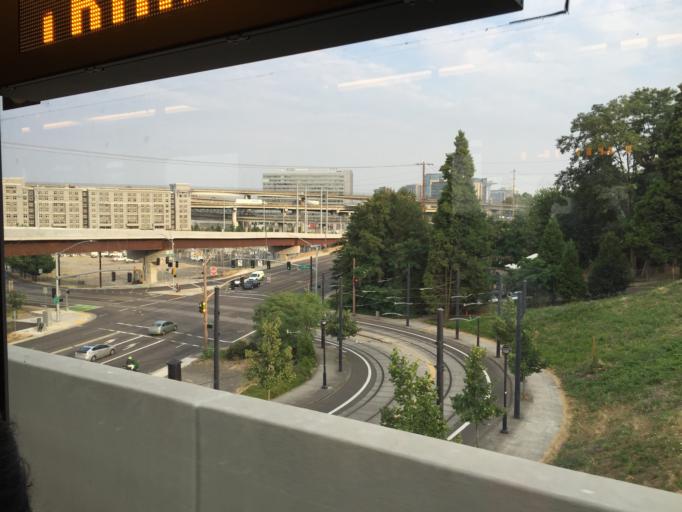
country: US
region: Oregon
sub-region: Multnomah County
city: Portland
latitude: 45.5080
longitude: -122.6769
